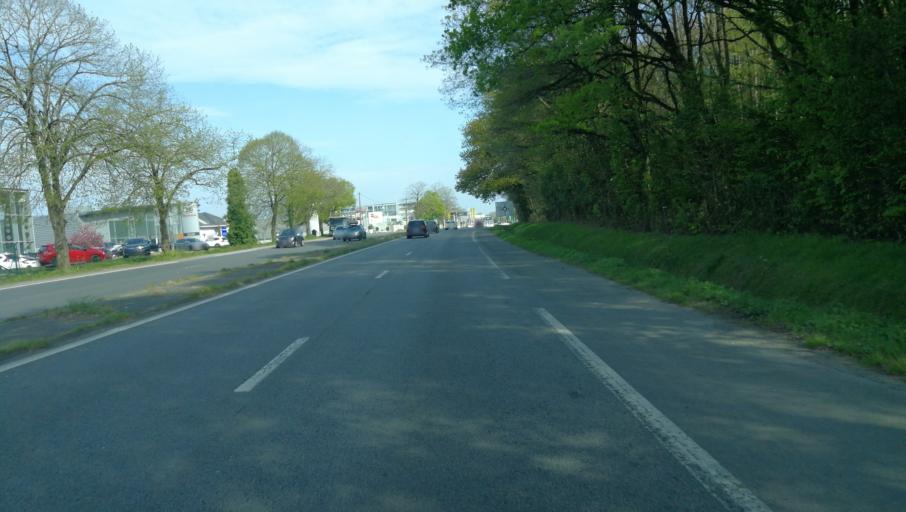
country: FR
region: Pays de la Loire
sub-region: Departement de la Loire-Atlantique
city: Orvault
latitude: 47.2556
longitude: -1.6337
